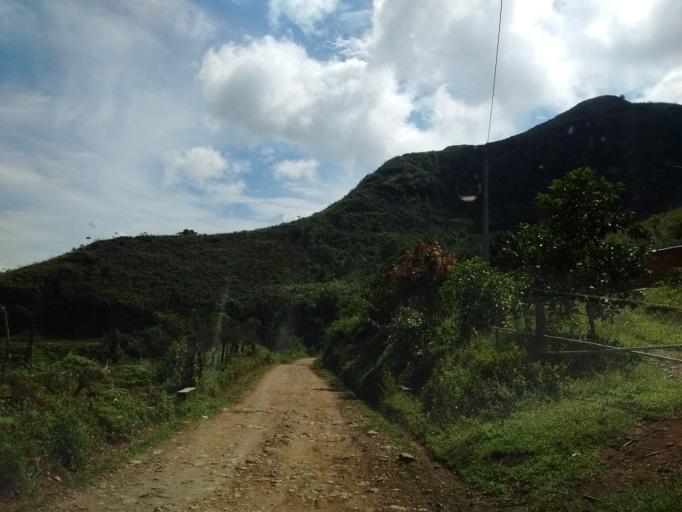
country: CO
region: Cauca
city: Morales
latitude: 2.6941
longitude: -76.7470
